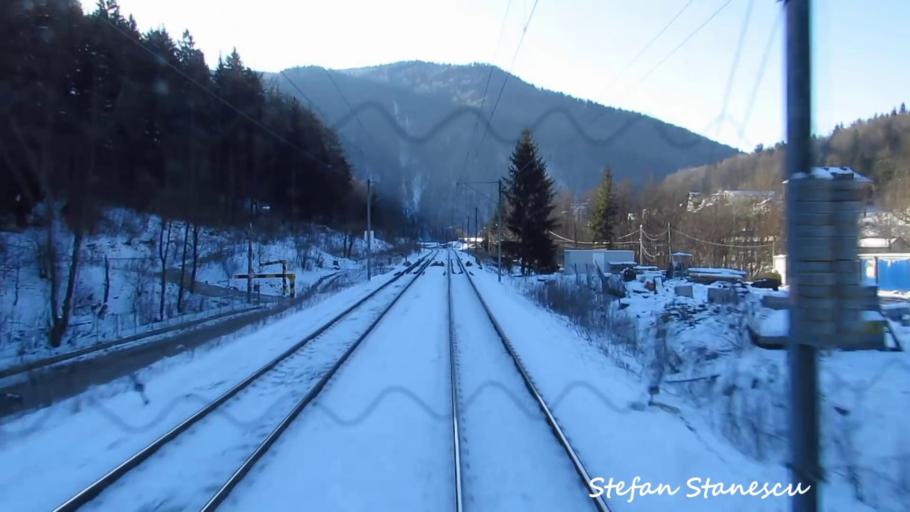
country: RO
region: Prahova
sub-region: Oras Sinaia
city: Sinaia
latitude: 45.3675
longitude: 25.5464
